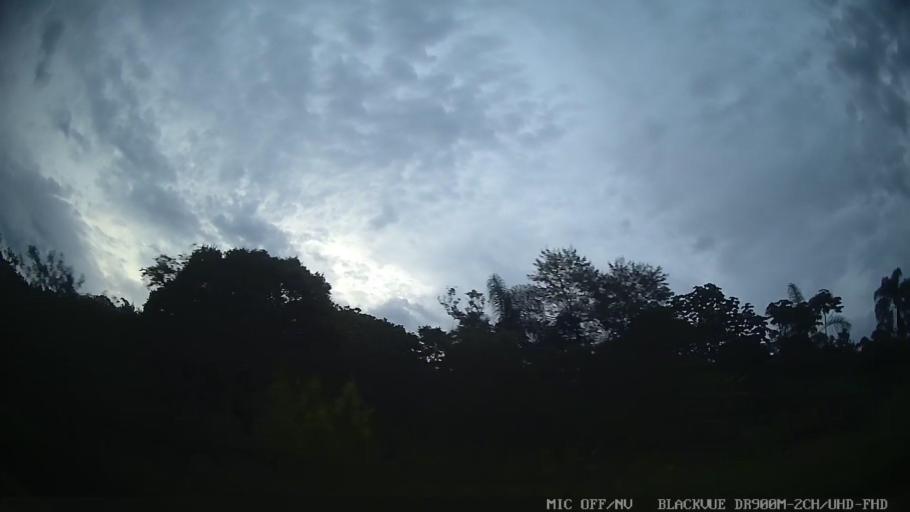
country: BR
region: Sao Paulo
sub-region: Amparo
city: Amparo
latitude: -22.8059
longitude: -46.7552
